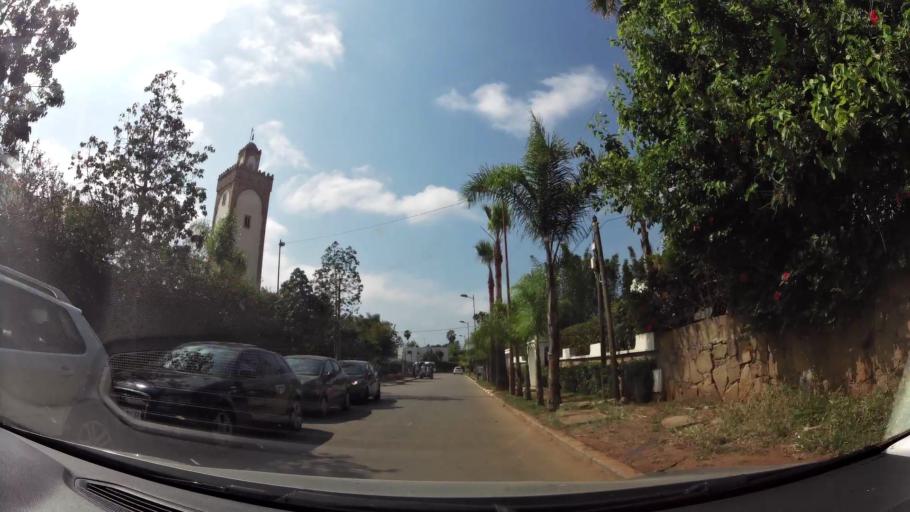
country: MA
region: Rabat-Sale-Zemmour-Zaer
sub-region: Rabat
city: Rabat
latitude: 33.9910
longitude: -6.8282
